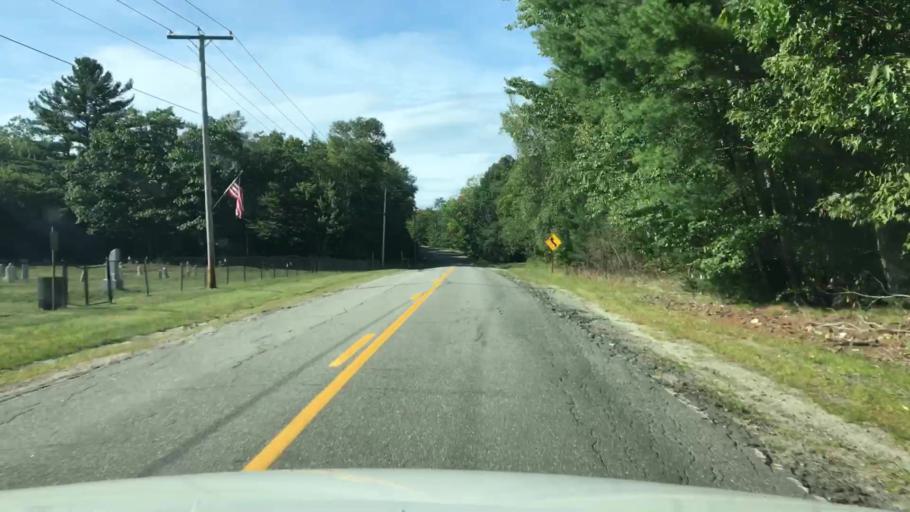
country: US
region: Maine
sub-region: Penobscot County
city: Enfield
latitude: 45.2224
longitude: -68.5376
